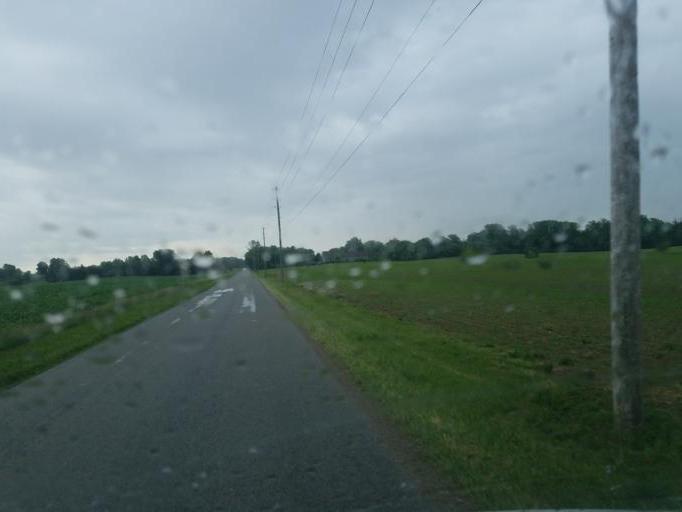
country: US
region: Ohio
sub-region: Morrow County
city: Mount Gilead
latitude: 40.5675
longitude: -82.8507
